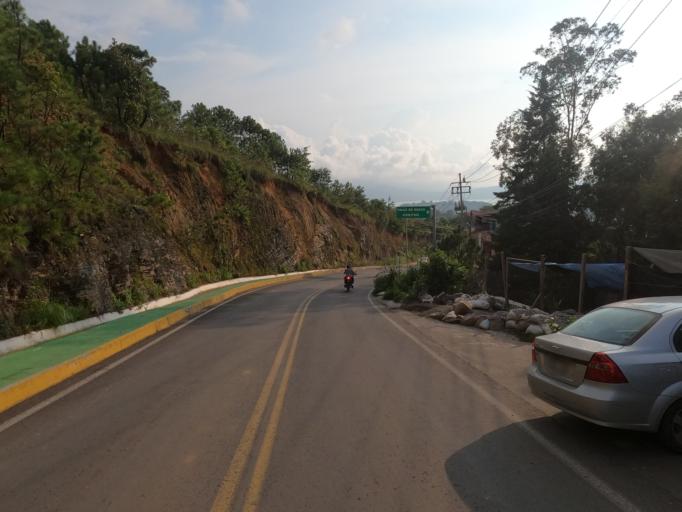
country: MX
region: Mexico
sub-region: Valle de Bravo
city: Colonia Rincon Villa del Valle
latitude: 19.2069
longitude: -100.1148
